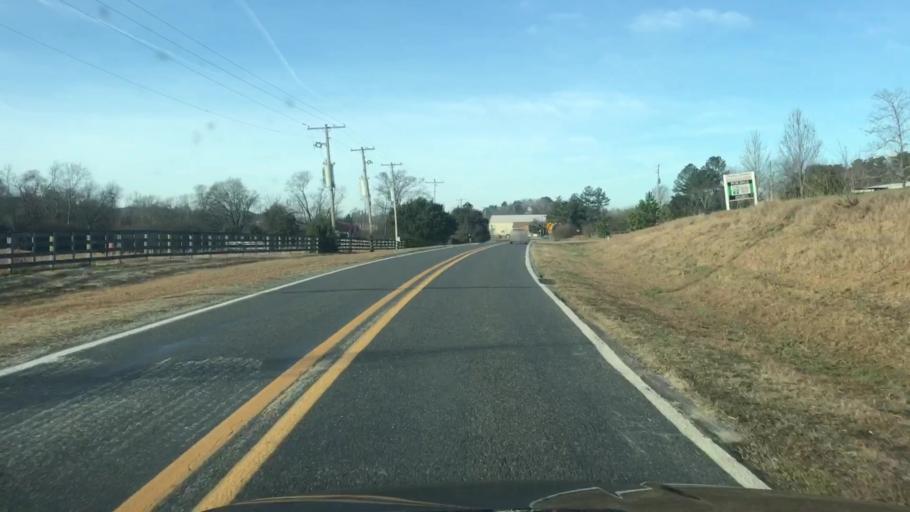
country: US
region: Arkansas
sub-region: Garland County
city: Rockwell
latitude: 34.4719
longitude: -93.2429
